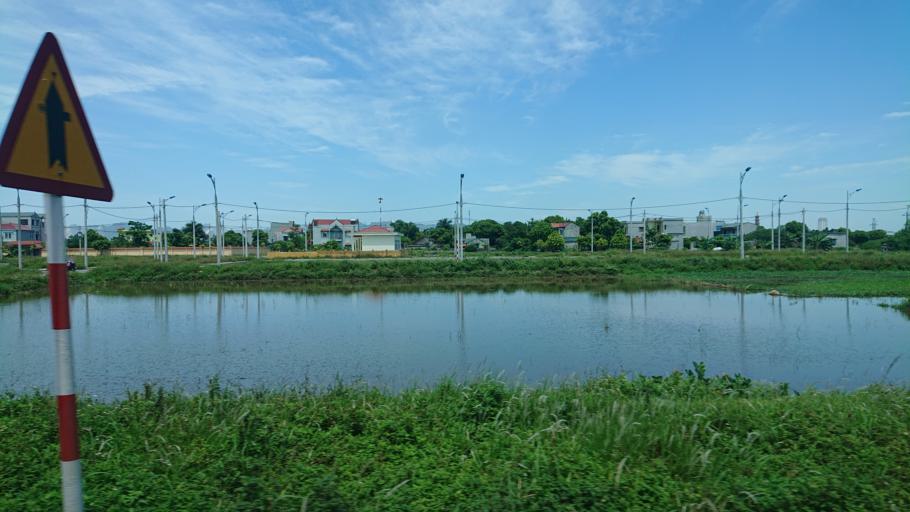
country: VN
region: Ha Nam
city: Thanh Pho Phu Ly
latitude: 20.5305
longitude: 105.9458
